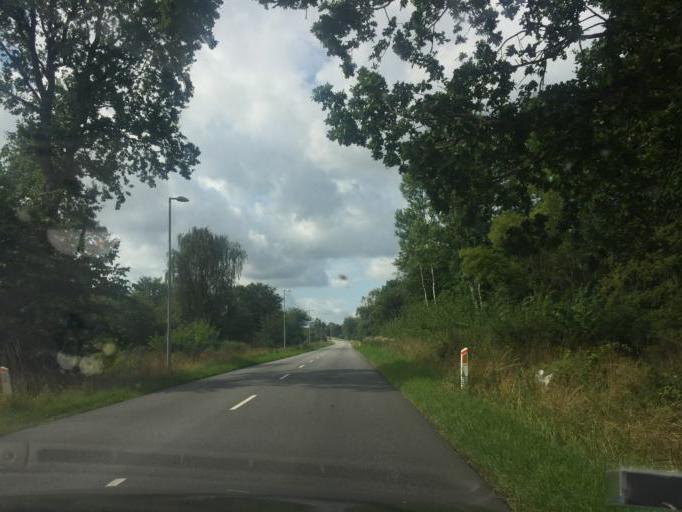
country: DK
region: Capital Region
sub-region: Allerod Kommune
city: Blovstrod
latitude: 55.8525
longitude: 12.3944
